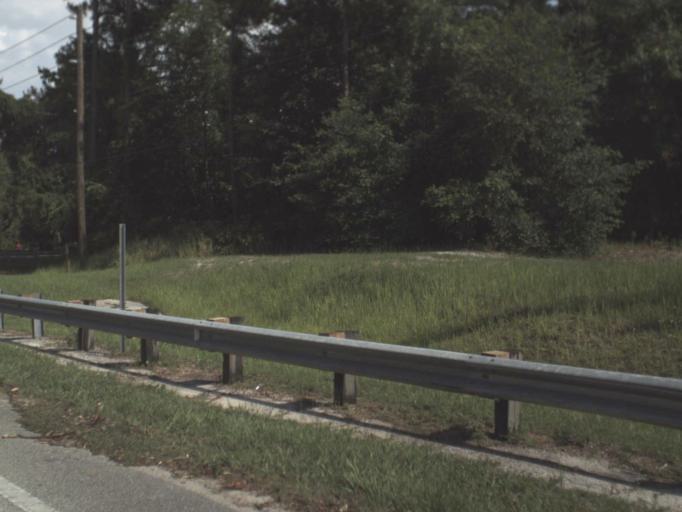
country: US
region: Florida
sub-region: Putnam County
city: Palatka
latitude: 29.6618
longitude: -81.6797
